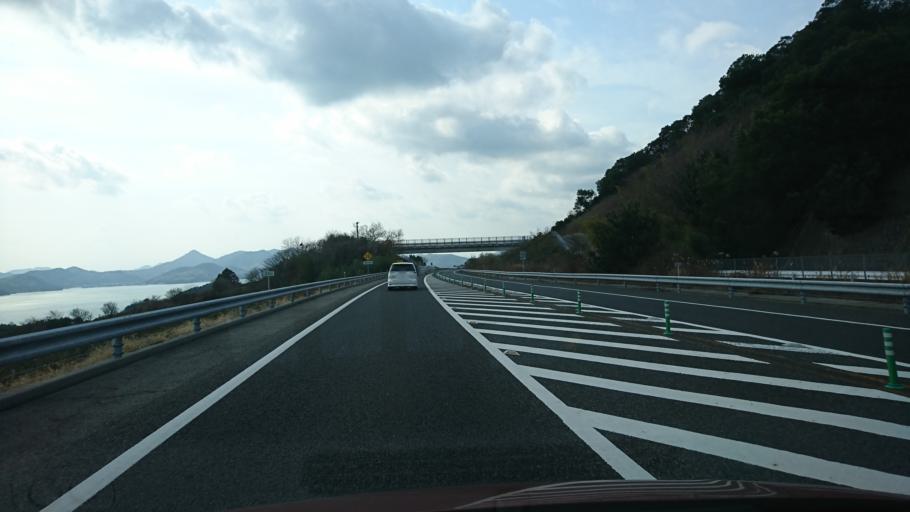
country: JP
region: Hiroshima
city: Innoshima
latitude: 34.2753
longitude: 133.1068
